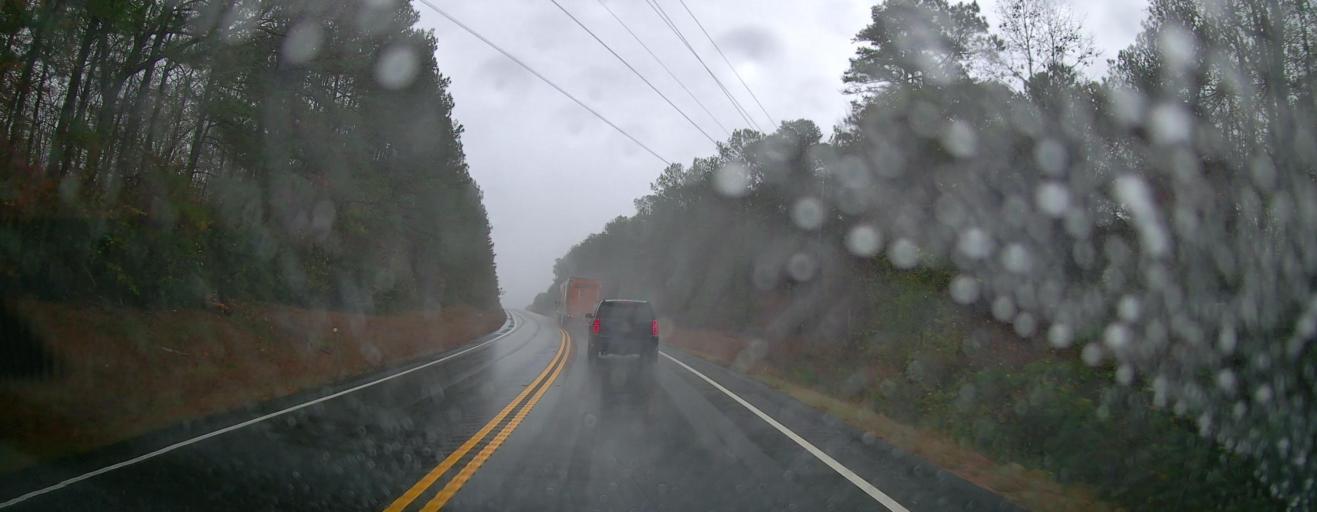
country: US
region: Georgia
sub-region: Putnam County
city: Eatonton
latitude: 33.1898
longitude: -83.4340
